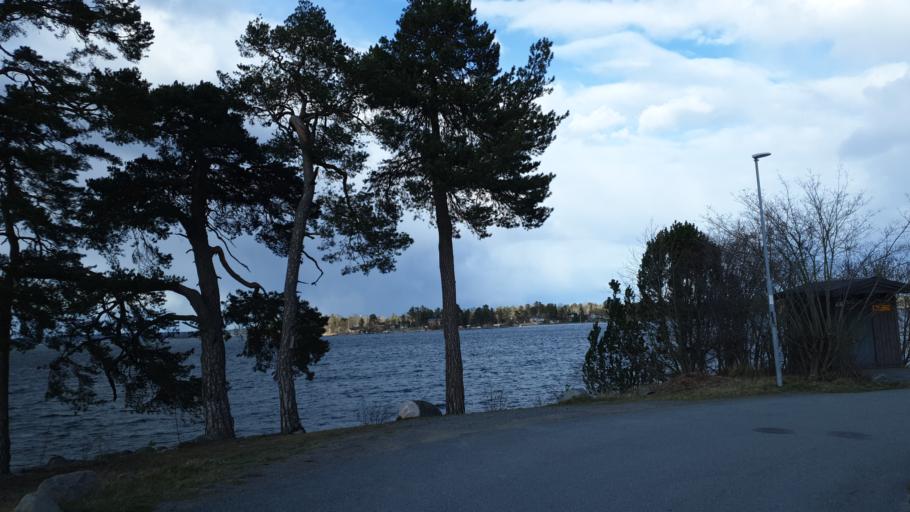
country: SE
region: Stockholm
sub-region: Lidingo
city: Lidingoe
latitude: 59.3912
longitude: 18.1180
